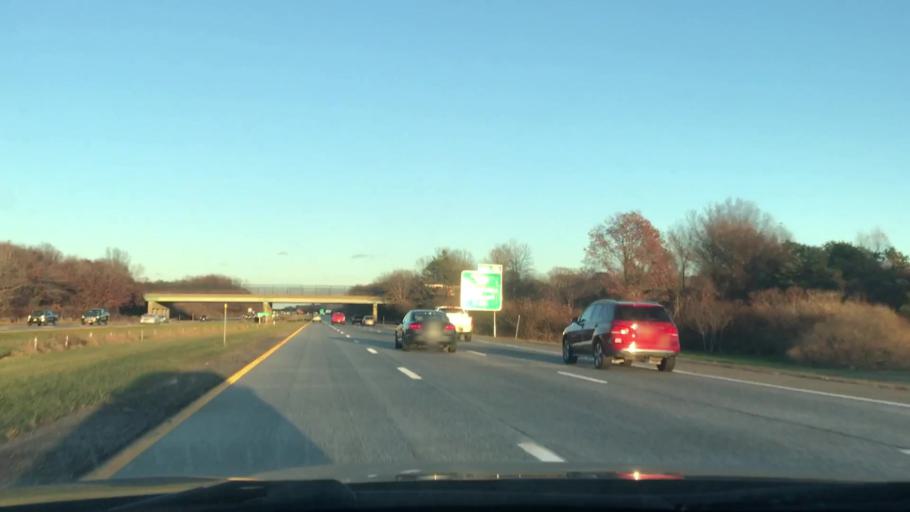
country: US
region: New York
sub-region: Suffolk County
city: Manorville
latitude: 40.8622
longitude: -72.8241
